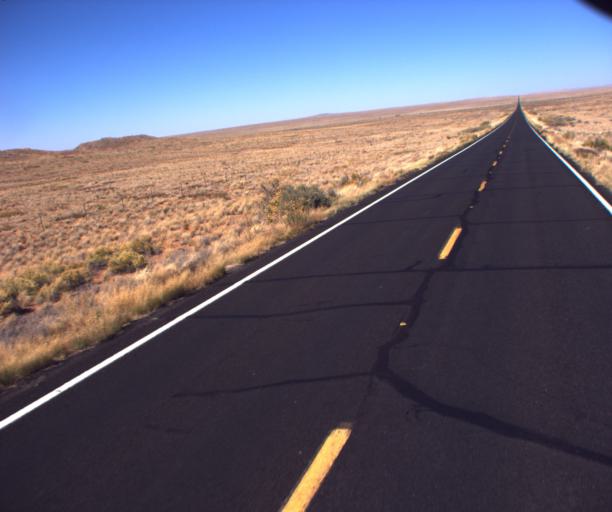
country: US
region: Arizona
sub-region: Navajo County
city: Dilkon
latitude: 35.5570
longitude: -110.4551
